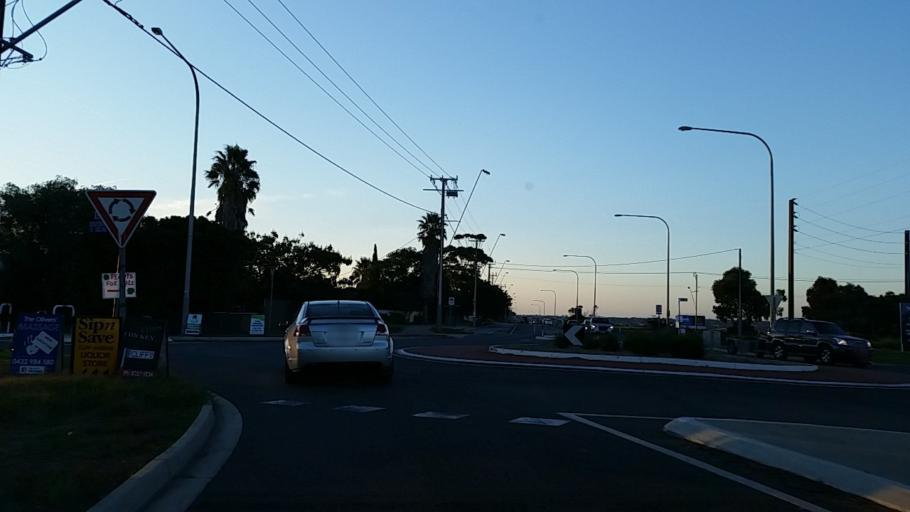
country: AU
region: South Australia
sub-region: Onkaparinga
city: Seaford
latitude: -35.1717
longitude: 138.4760
